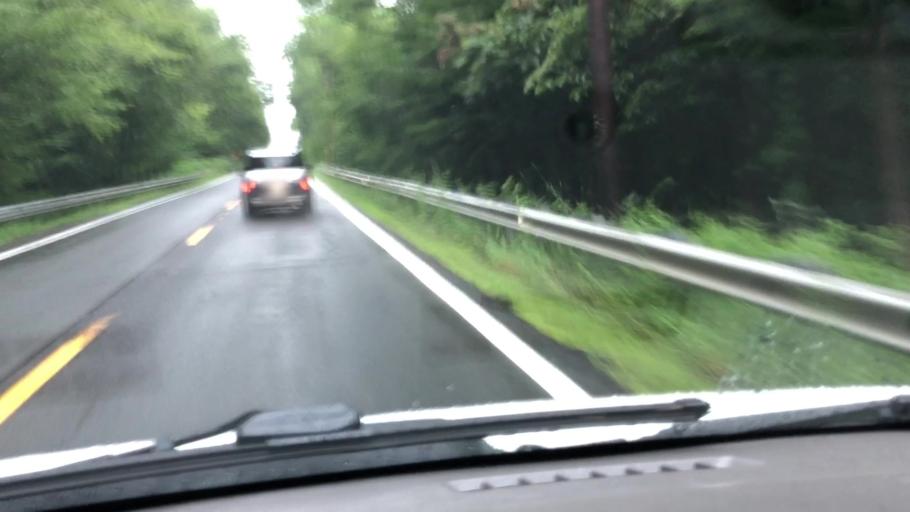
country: US
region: Massachusetts
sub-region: Hampshire County
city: Chesterfield
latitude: 42.3767
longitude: -72.9193
